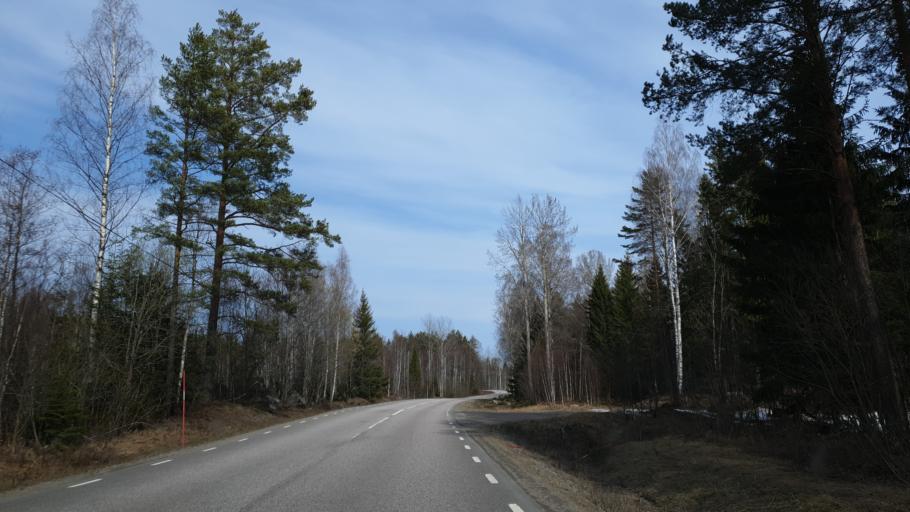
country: SE
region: Gaevleborg
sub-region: Gavle Kommun
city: Norrsundet
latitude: 60.9628
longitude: 17.0428
